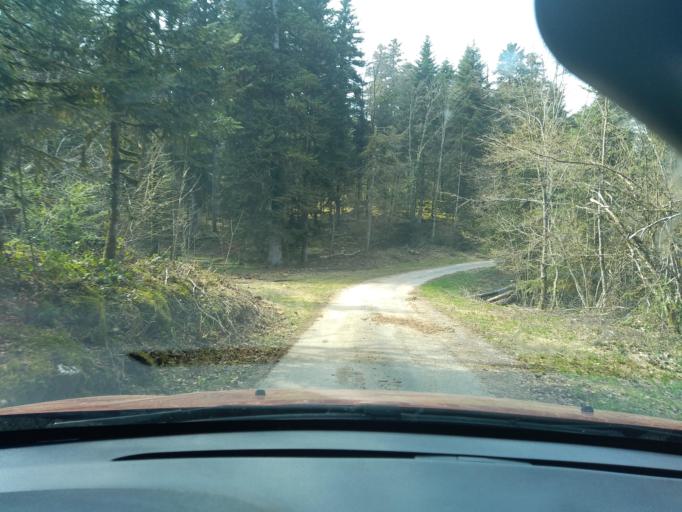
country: FR
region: Franche-Comte
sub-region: Departement du Jura
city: Moirans-en-Montagne
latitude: 46.4722
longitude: 5.7583
